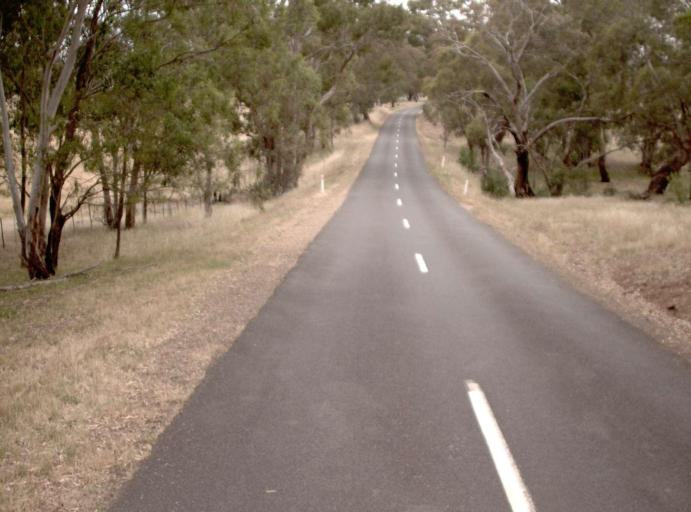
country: AU
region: Victoria
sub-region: Wellington
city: Heyfield
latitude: -37.6544
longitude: 146.6424
